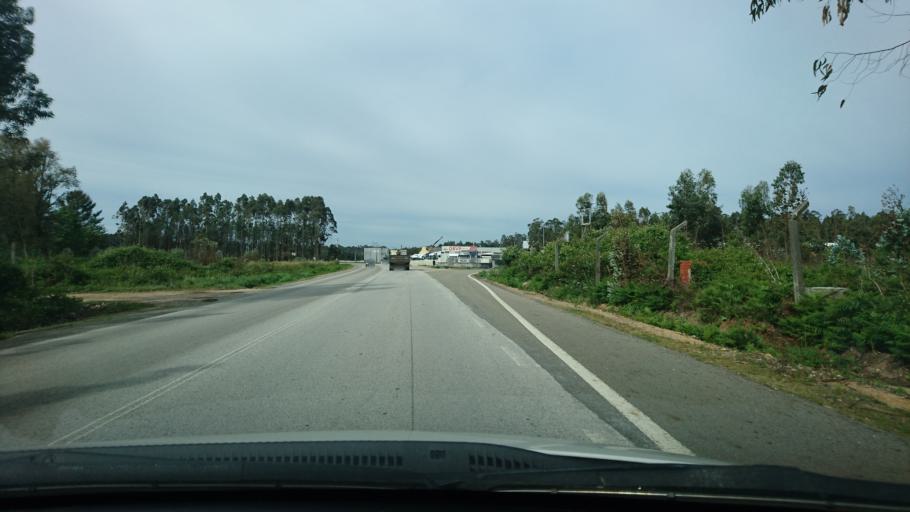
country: PT
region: Aveiro
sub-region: Albergaria-A-Velha
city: Albergaria-a-Velha
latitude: 40.7003
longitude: -8.5051
